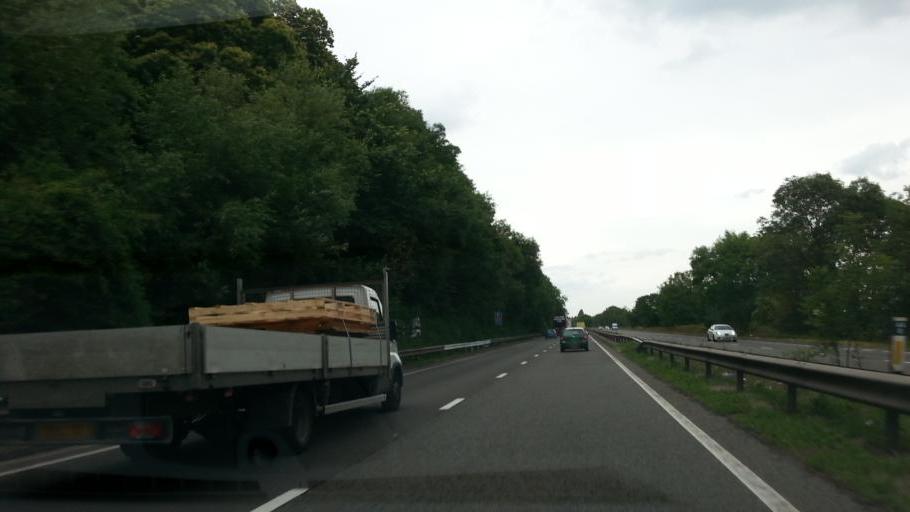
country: GB
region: England
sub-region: Herefordshire
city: Walford
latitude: 51.8994
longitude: -2.6290
